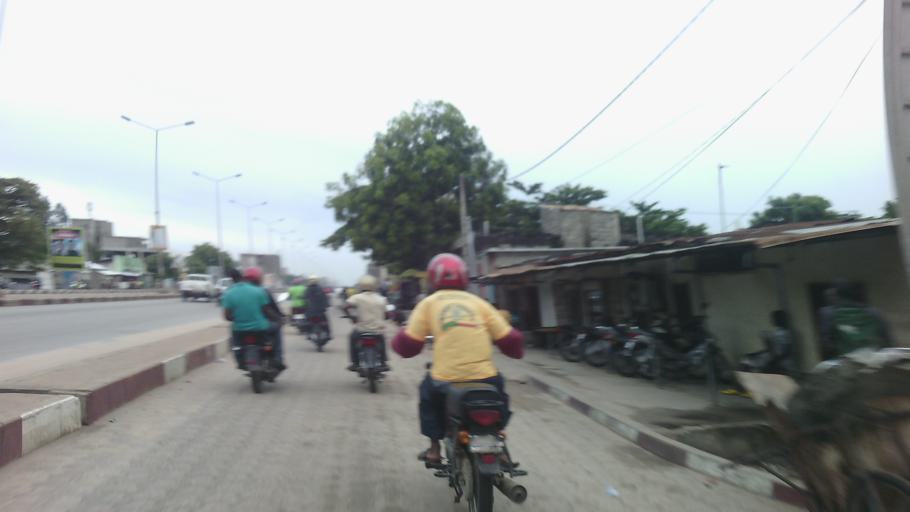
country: BJ
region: Littoral
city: Cotonou
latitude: 6.3672
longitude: 2.4141
